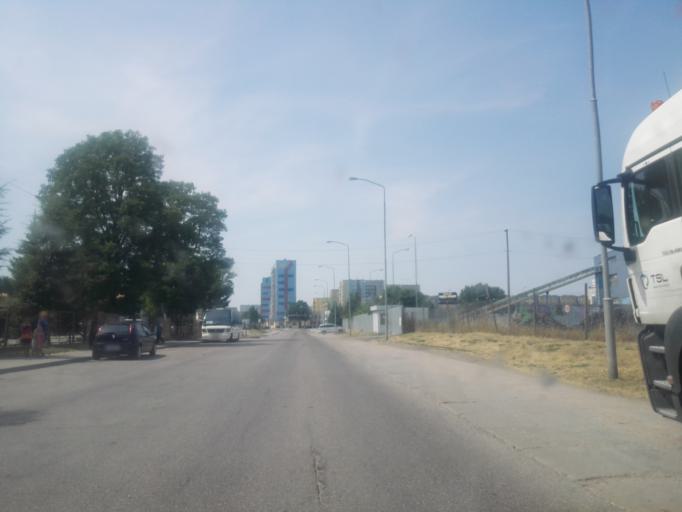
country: PL
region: Podlasie
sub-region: Suwalki
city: Suwalki
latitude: 54.1040
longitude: 22.9421
